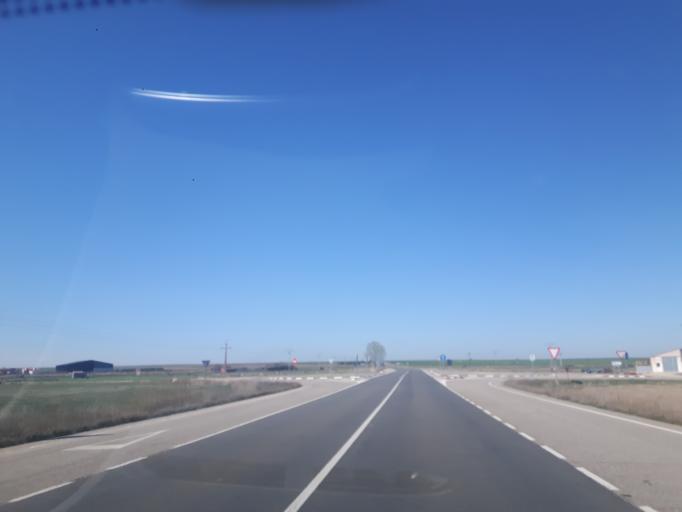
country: ES
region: Castille and Leon
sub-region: Provincia de Salamanca
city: Nava de Sotrobal
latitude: 40.8874
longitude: -5.2860
